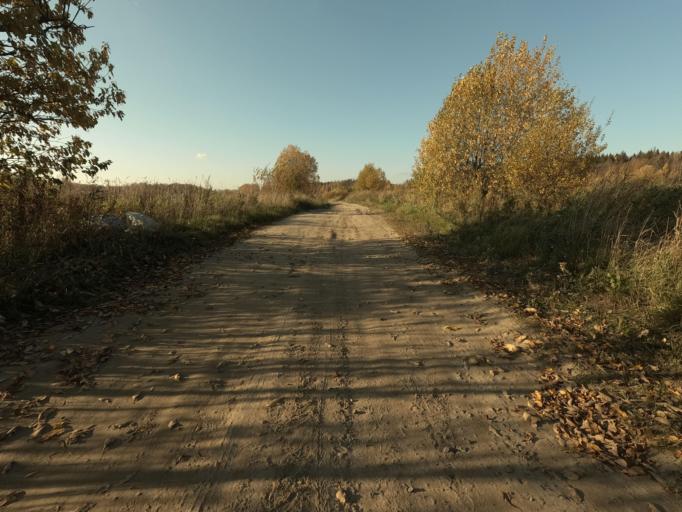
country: RU
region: Leningrad
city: Luppolovo
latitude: 60.1438
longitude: 30.2471
